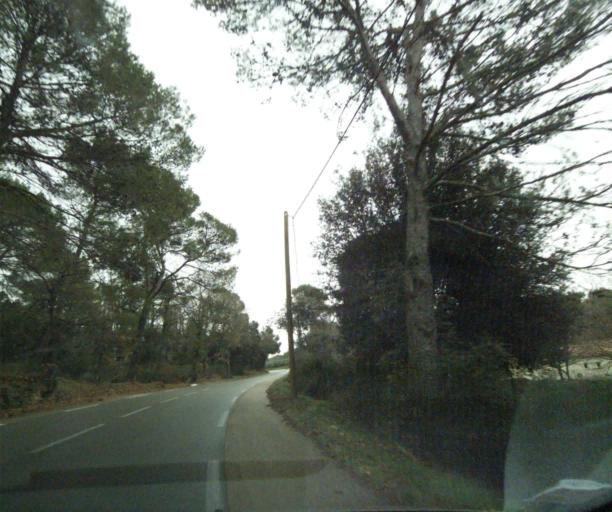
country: FR
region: Provence-Alpes-Cote d'Azur
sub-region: Departement des Bouches-du-Rhone
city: Rognes
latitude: 43.6621
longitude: 5.3692
